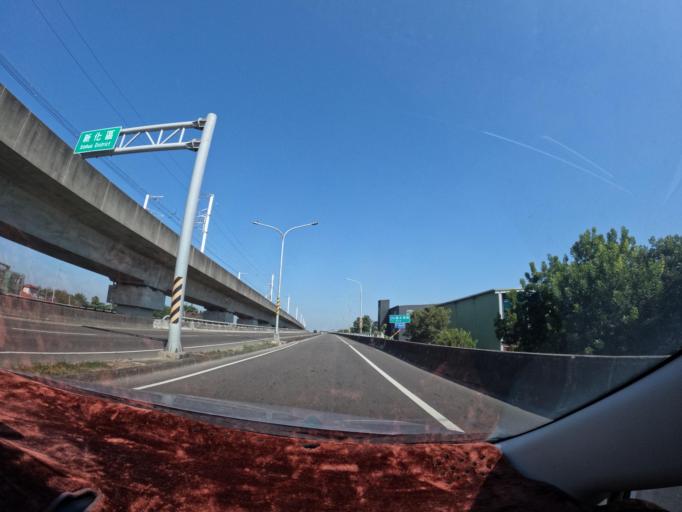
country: TW
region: Taiwan
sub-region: Tainan
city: Tainan
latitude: 23.0163
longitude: 120.2886
